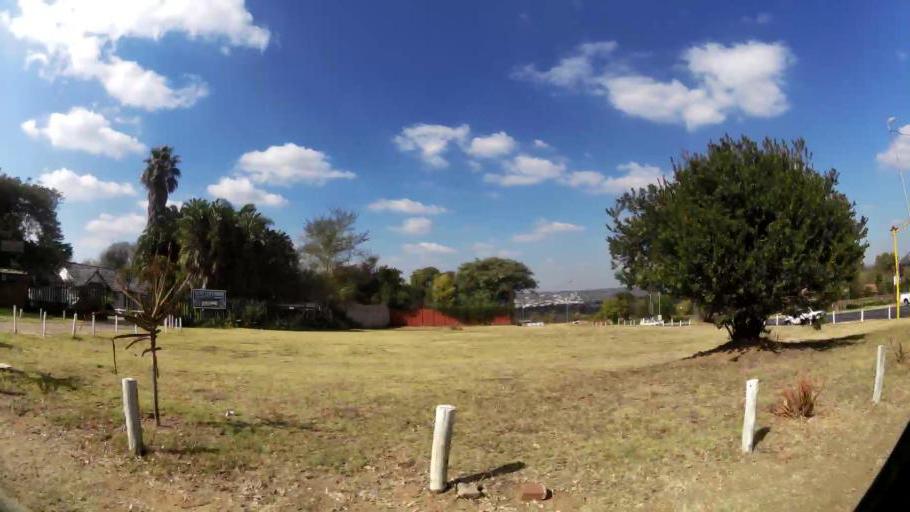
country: ZA
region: Gauteng
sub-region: West Rand District Municipality
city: Muldersdriseloop
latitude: -26.0649
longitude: 27.9597
